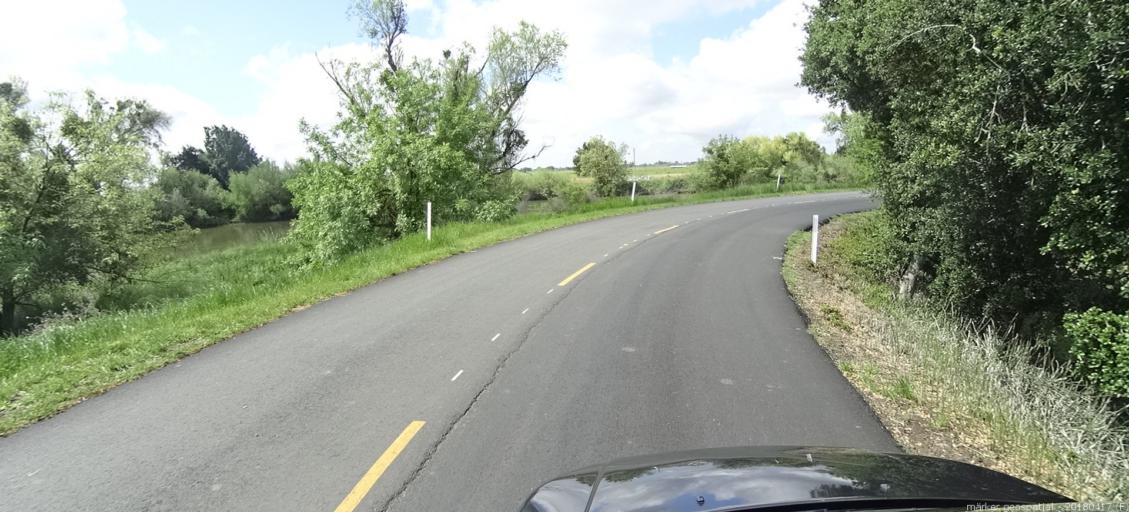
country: US
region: California
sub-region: Sacramento County
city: Walnut Grove
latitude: 38.2268
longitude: -121.5273
